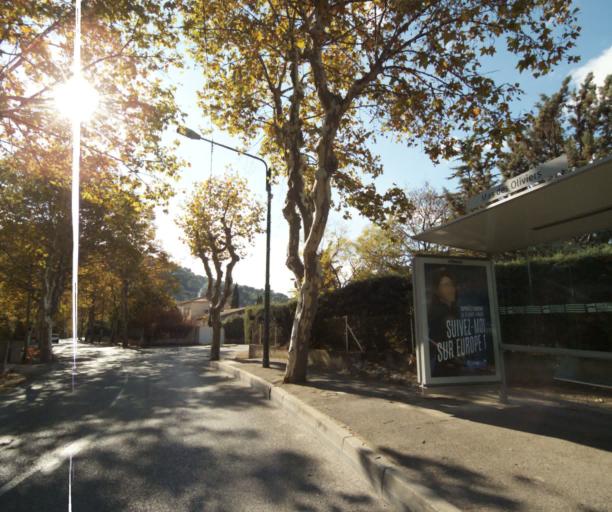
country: FR
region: Provence-Alpes-Cote d'Azur
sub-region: Departement des Bouches-du-Rhone
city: Allauch
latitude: 43.3615
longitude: 5.4938
